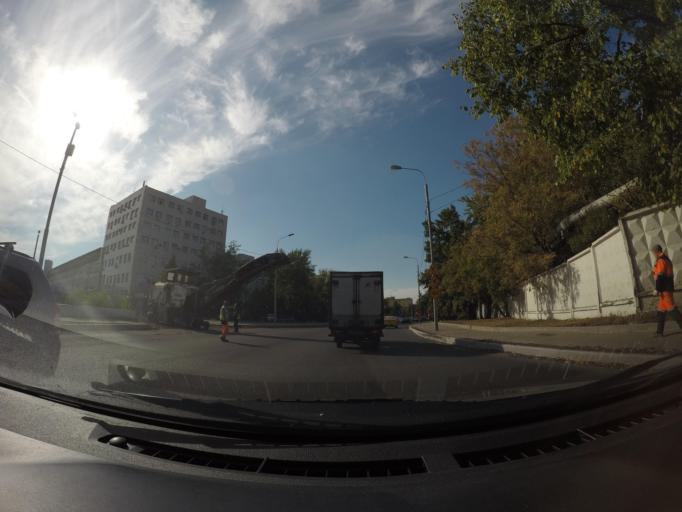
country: RU
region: Moscow
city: Mar'ina Roshcha
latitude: 55.8097
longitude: 37.6091
